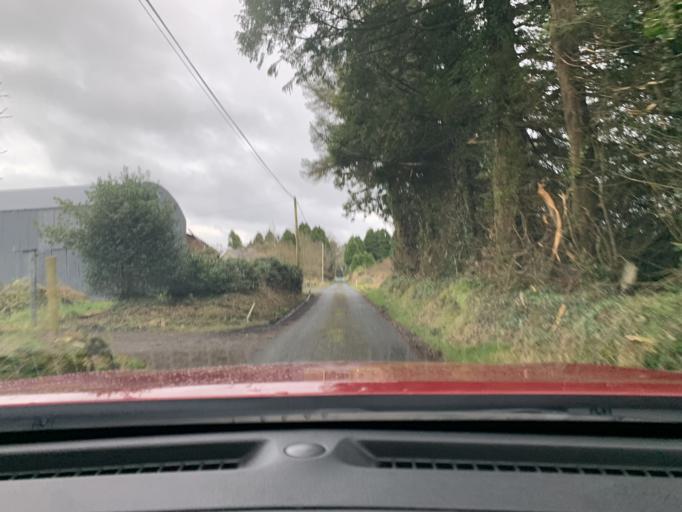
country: IE
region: Connaught
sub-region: Roscommon
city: Ballaghaderreen
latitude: 53.9655
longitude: -8.5099
